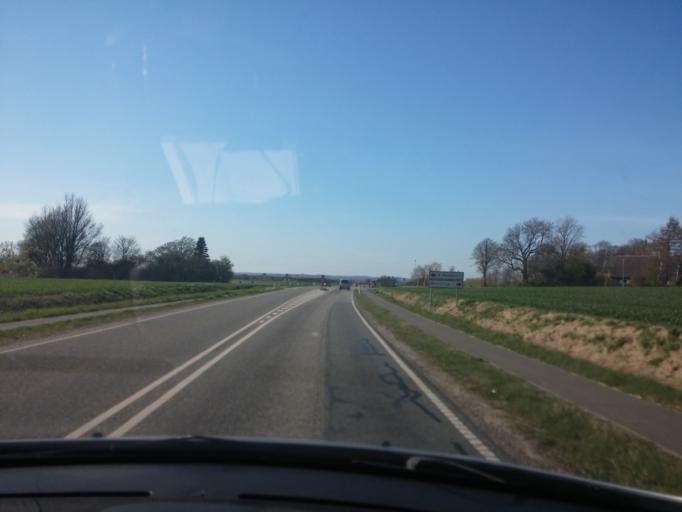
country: DK
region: Central Jutland
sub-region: Odder Kommune
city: Odder
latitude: 55.9397
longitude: 10.2132
